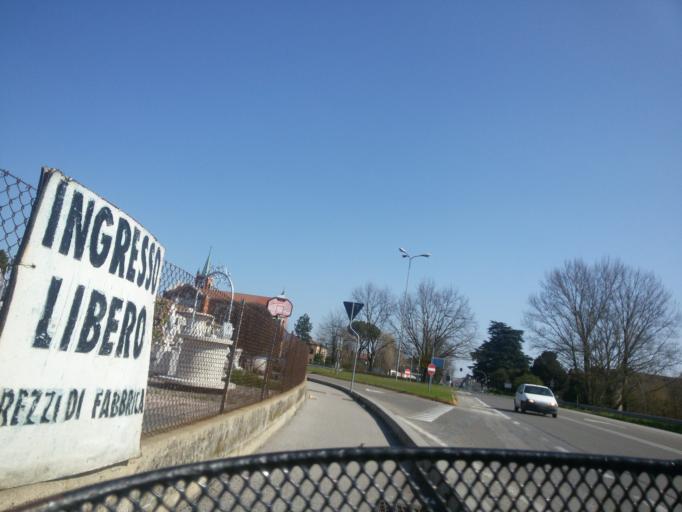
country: IT
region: Emilia-Romagna
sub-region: Provincia di Ravenna
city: Lugo
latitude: 44.4280
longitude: 11.8931
